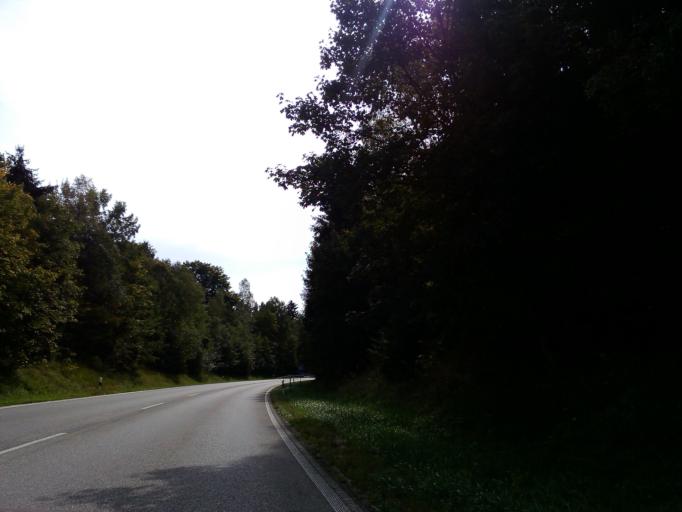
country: DE
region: Bavaria
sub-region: Upper Bavaria
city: Pocking
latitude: 47.9949
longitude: 11.3085
